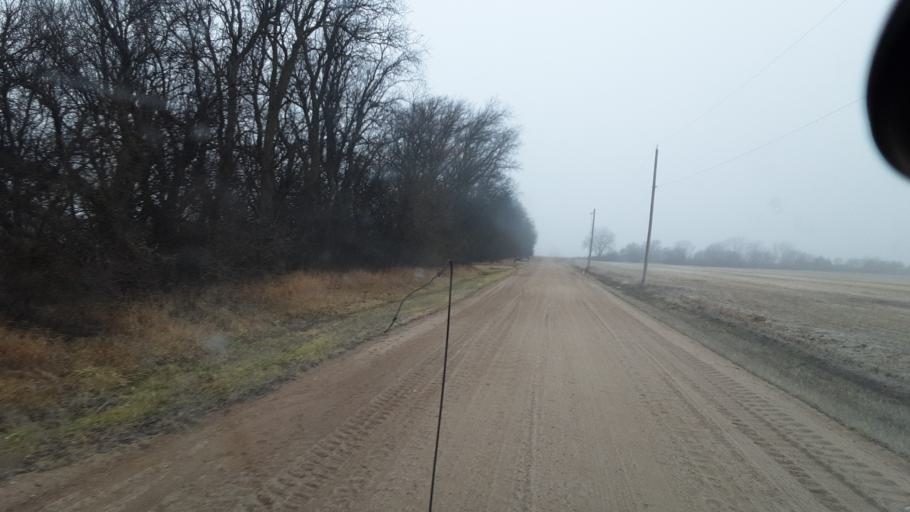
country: US
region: Kansas
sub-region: Reno County
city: South Hutchinson
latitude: 37.9555
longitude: -97.9447
